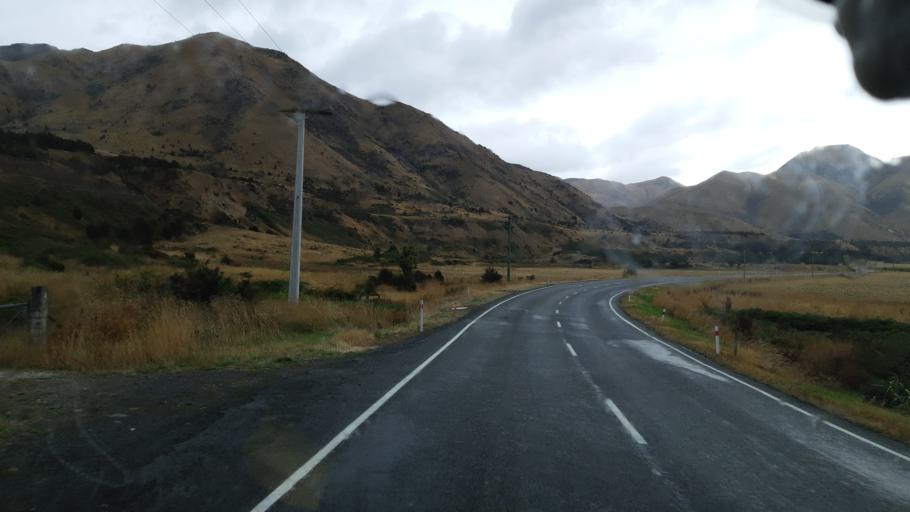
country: NZ
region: Canterbury
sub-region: Hurunui District
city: Amberley
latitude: -42.6283
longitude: 172.7694
